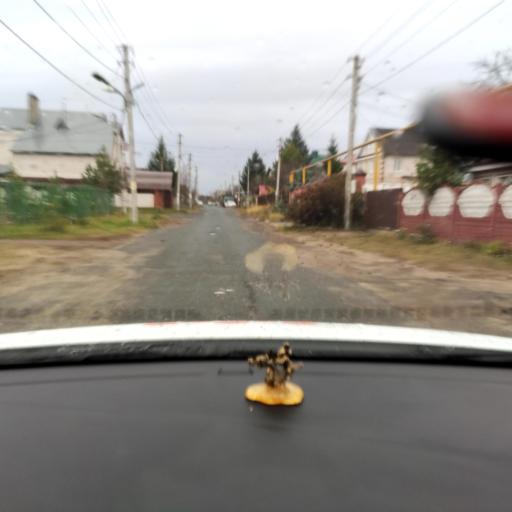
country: RU
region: Tatarstan
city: Vysokaya Gora
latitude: 55.8453
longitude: 49.2384
